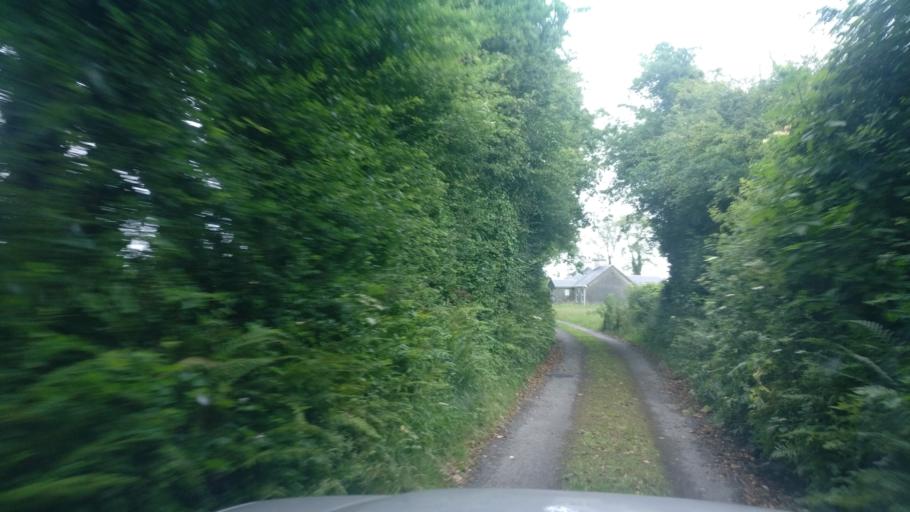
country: IE
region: Connaught
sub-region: County Galway
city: Ballinasloe
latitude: 53.2949
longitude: -8.3486
